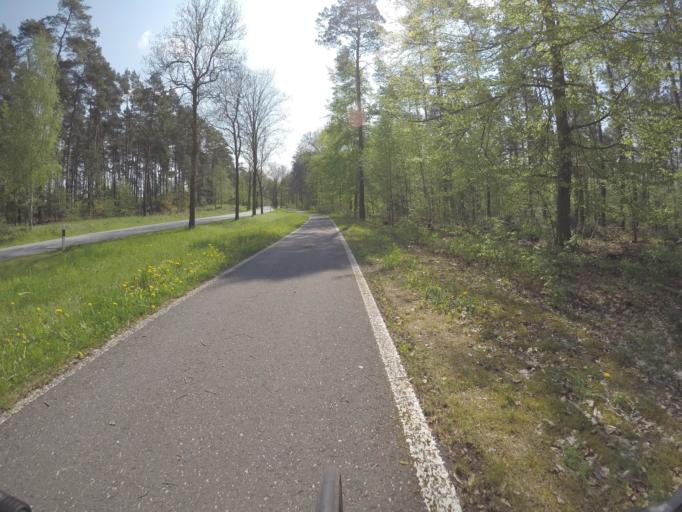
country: DE
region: Brandenburg
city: Wandlitz
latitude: 52.7951
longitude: 13.5207
